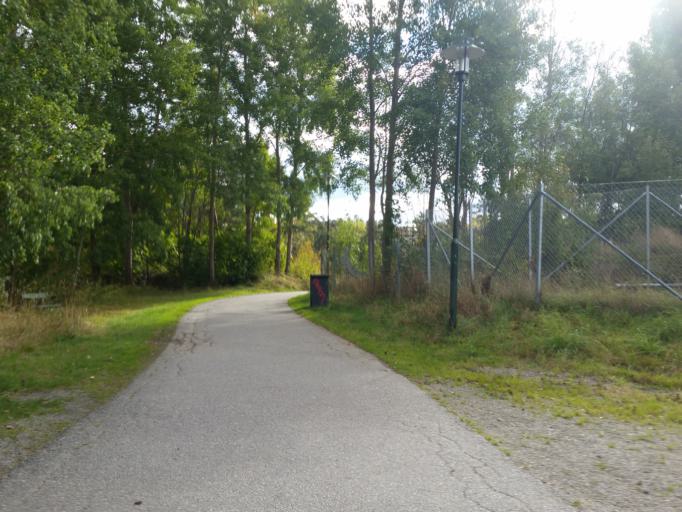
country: SE
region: Stockholm
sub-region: Stockholms Kommun
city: OEstermalm
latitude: 59.2897
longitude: 18.1080
